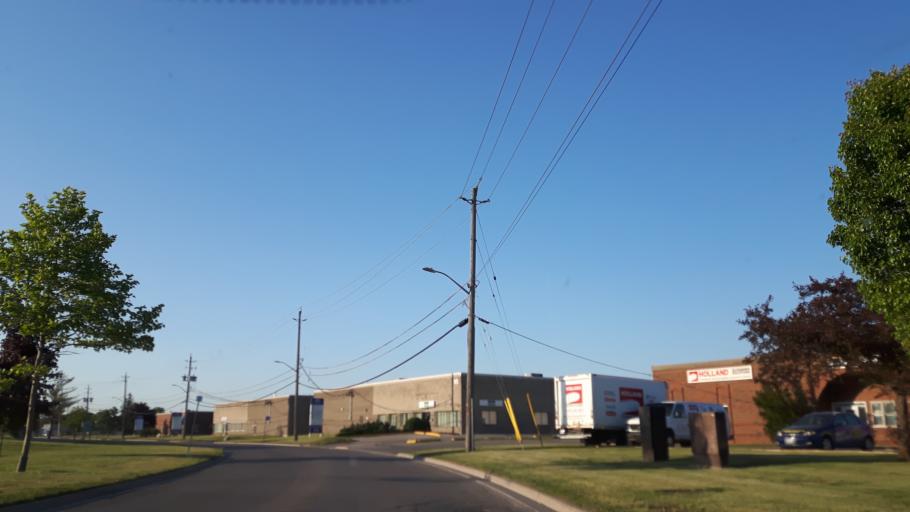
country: CA
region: Ontario
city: London
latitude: 42.9305
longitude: -81.2119
